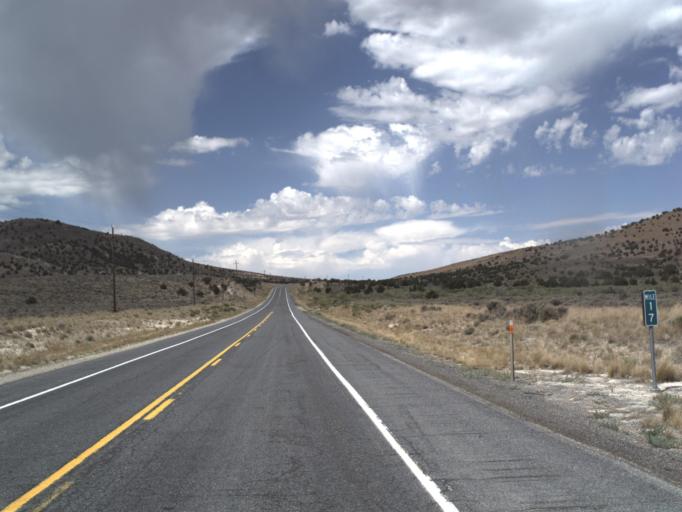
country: US
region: Utah
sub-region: Utah County
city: Eagle Mountain
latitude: 40.0756
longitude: -112.3523
